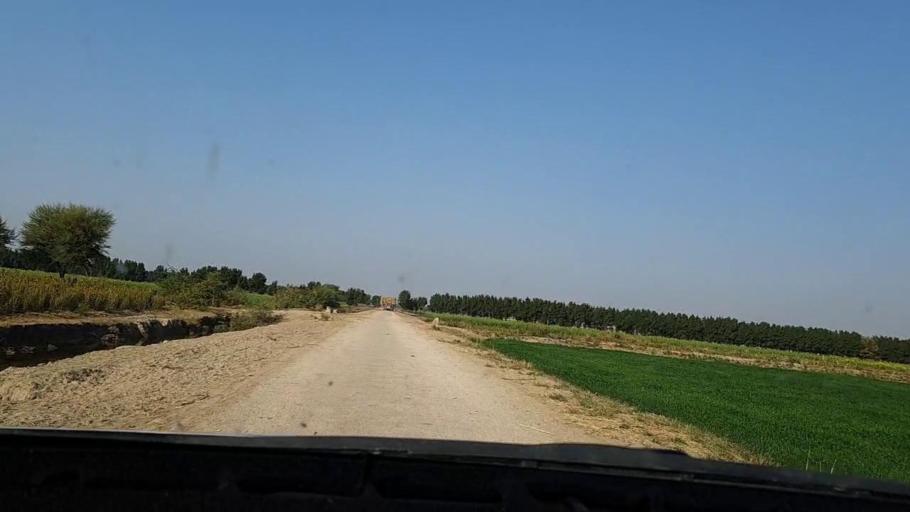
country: PK
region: Sindh
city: Tando Mittha Khan
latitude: 25.8233
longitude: 69.3063
